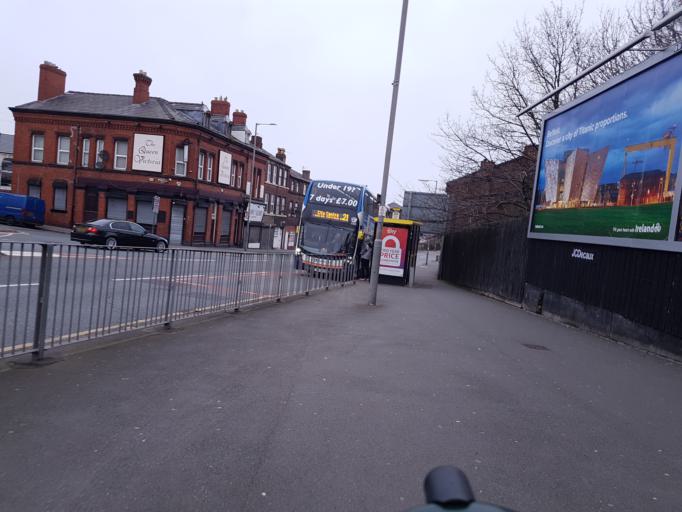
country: GB
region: England
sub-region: Sefton
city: Litherland
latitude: 53.4482
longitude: -2.9666
